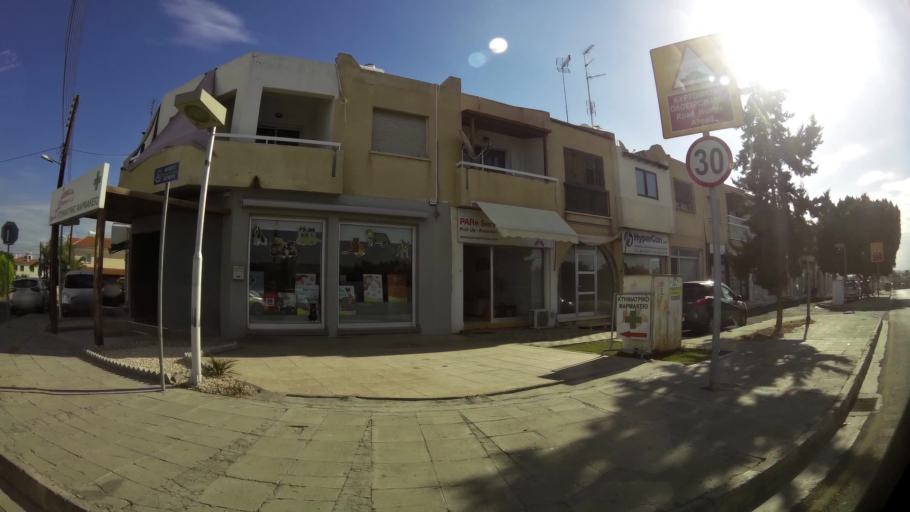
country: CY
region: Lefkosia
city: Nicosia
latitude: 35.1323
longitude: 33.3597
